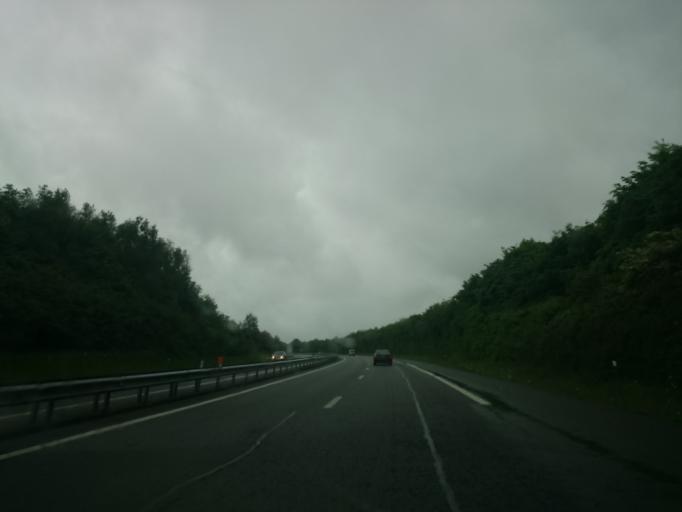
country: FR
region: Brittany
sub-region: Departement d'Ille-et-Vilaine
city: Plelan-le-Grand
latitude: 47.9978
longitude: -2.0954
